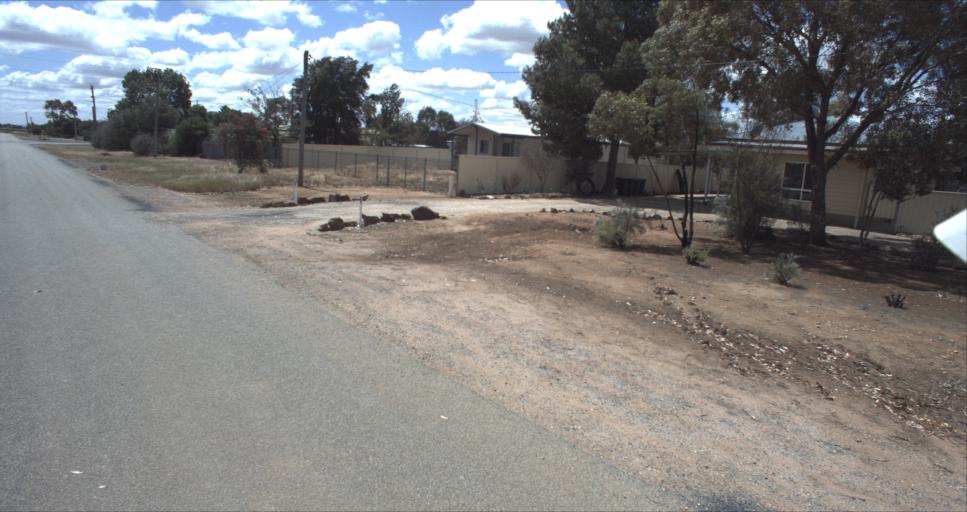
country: AU
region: New South Wales
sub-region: Murrumbidgee Shire
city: Darlington Point
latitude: -34.5132
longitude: 146.1844
